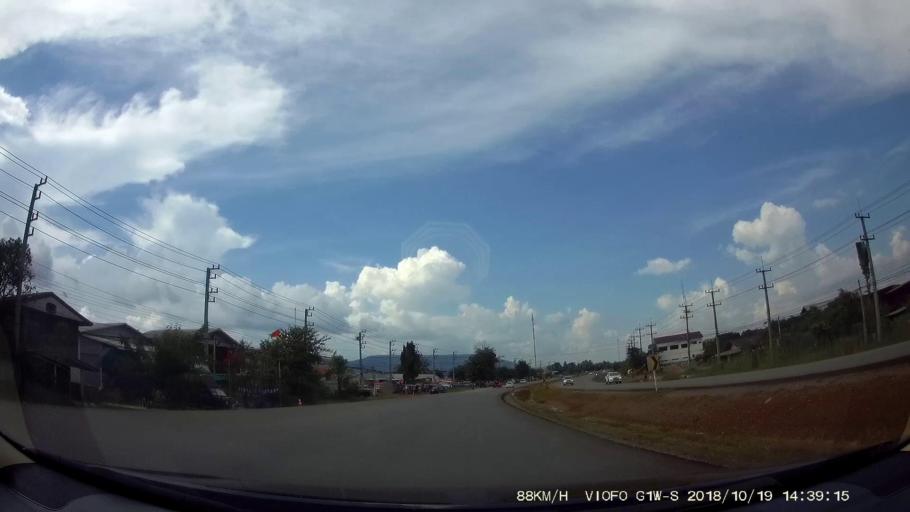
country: TH
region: Chaiyaphum
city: Kaeng Khro
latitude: 16.2238
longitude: 102.1960
